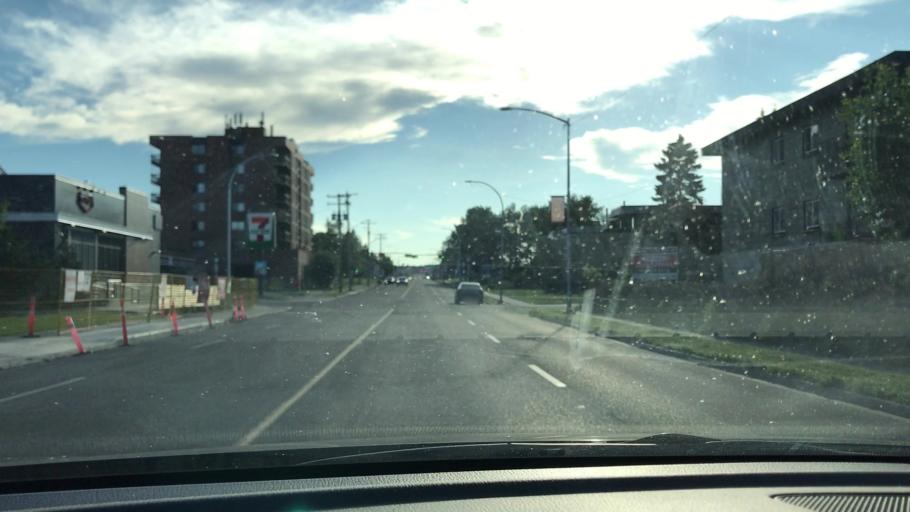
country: CA
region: Alberta
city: Calgary
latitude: 51.0379
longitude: -114.1273
